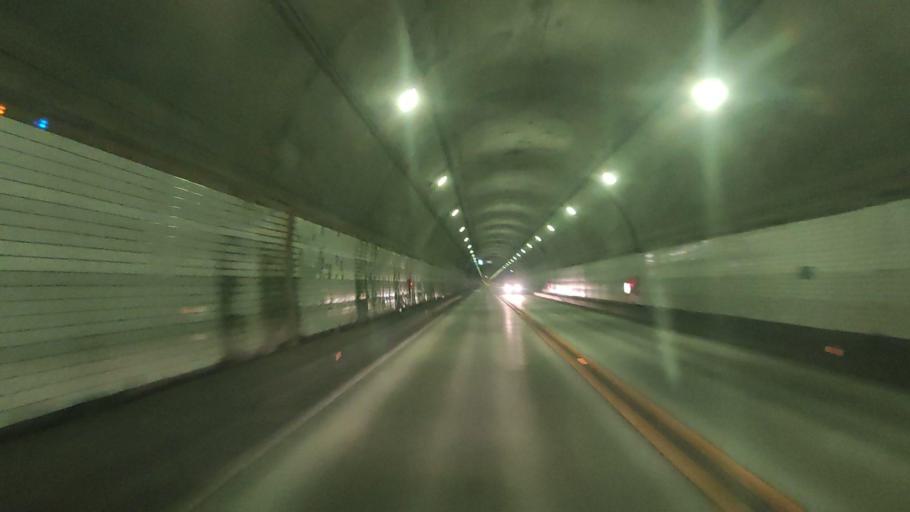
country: JP
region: Fukuoka
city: Maebaru-chuo
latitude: 33.4730
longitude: 130.2844
